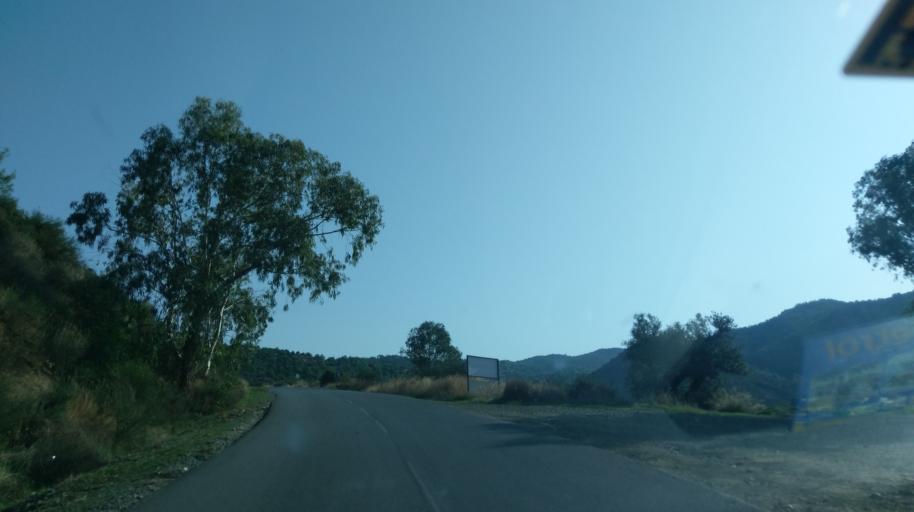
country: CY
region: Lefkosia
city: Kato Pyrgos
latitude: 35.1642
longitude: 32.7495
